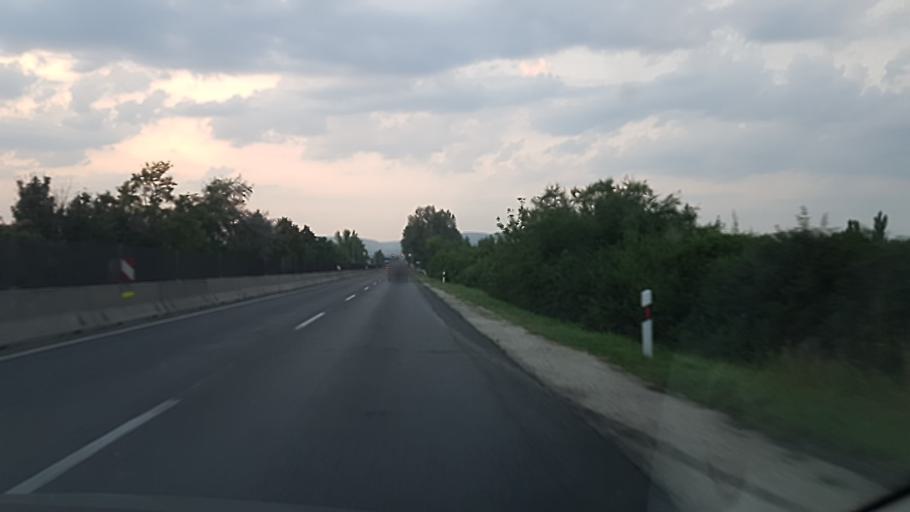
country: HU
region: Pest
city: Budakalasz
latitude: 47.6382
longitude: 19.0693
